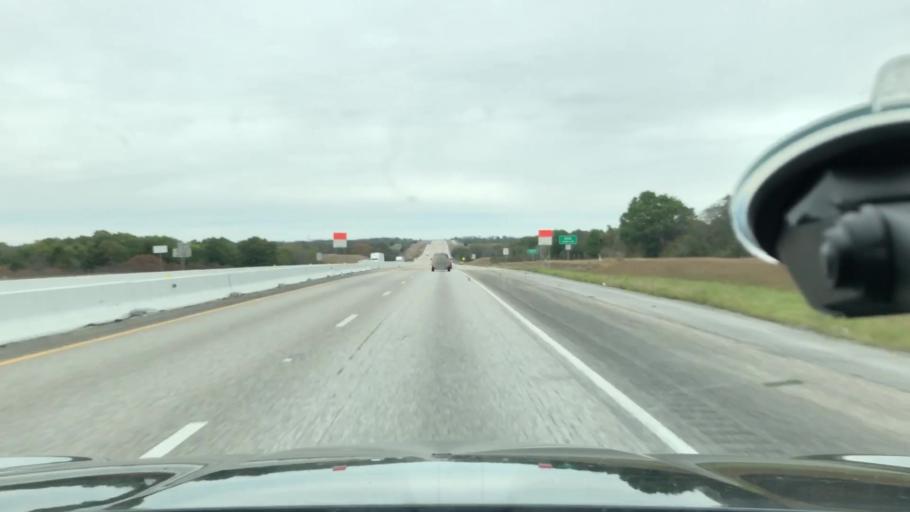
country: US
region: Texas
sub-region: Ellis County
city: Plum Grove
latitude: 32.1172
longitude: -96.9865
